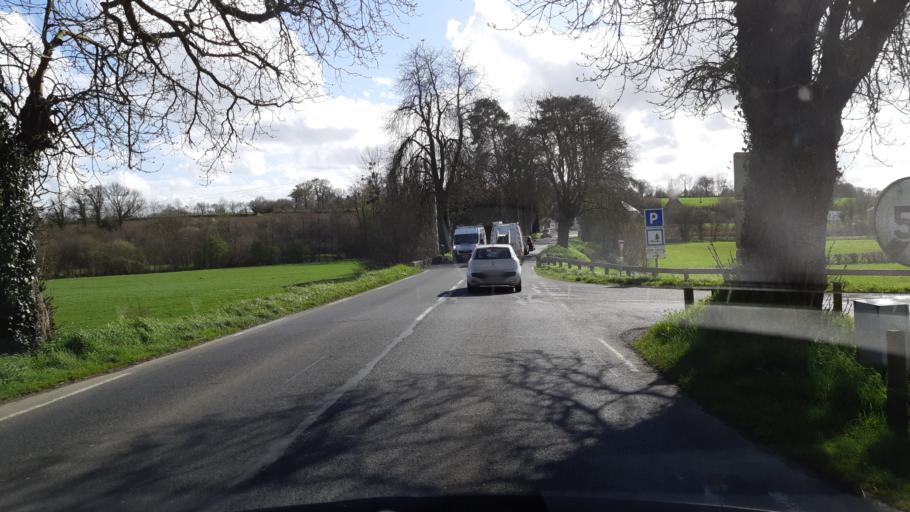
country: FR
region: Lower Normandy
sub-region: Departement de la Manche
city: Agneaux
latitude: 49.0915
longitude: -1.1177
